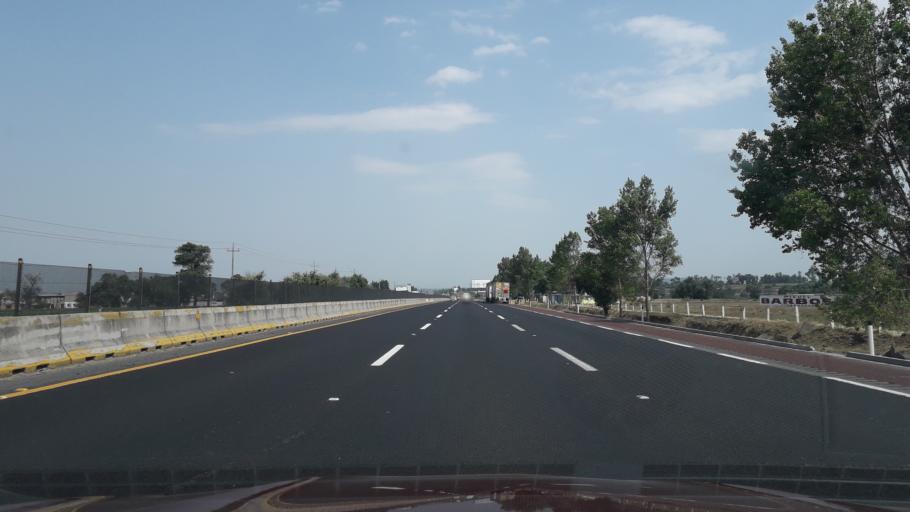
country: MX
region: Puebla
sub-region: San Salvador el Verde
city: San Lucas el Grande
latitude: 19.3033
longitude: -98.4871
